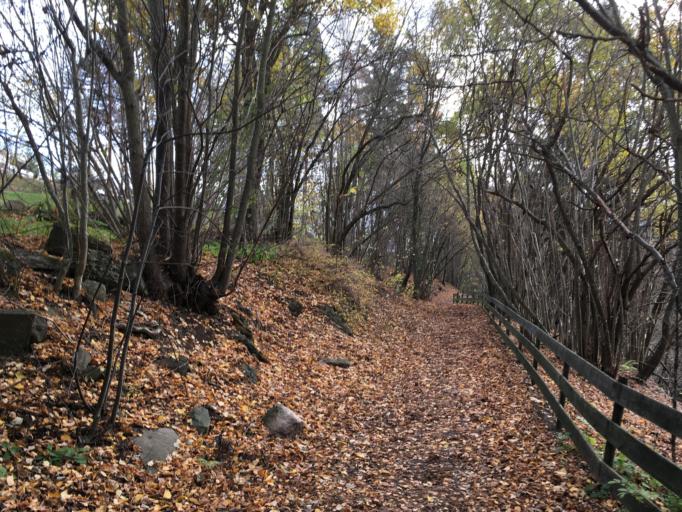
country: NO
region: Akershus
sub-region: Baerum
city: Lysaker
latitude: 59.9370
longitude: 10.6351
